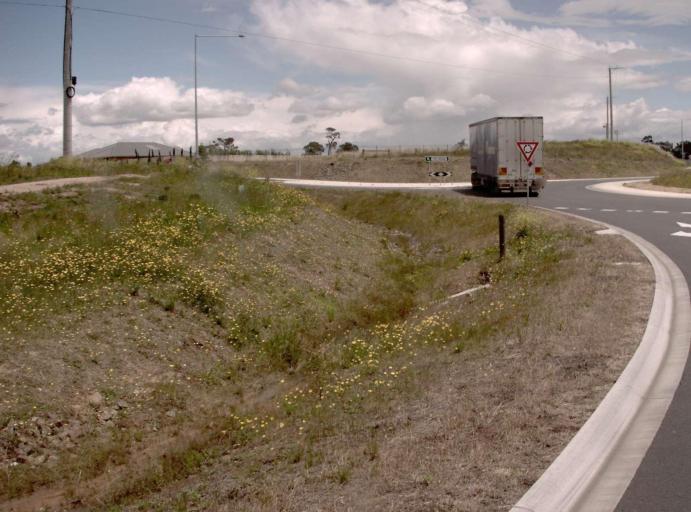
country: AU
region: Victoria
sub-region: Wellington
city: Sale
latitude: -38.1088
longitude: 147.0383
